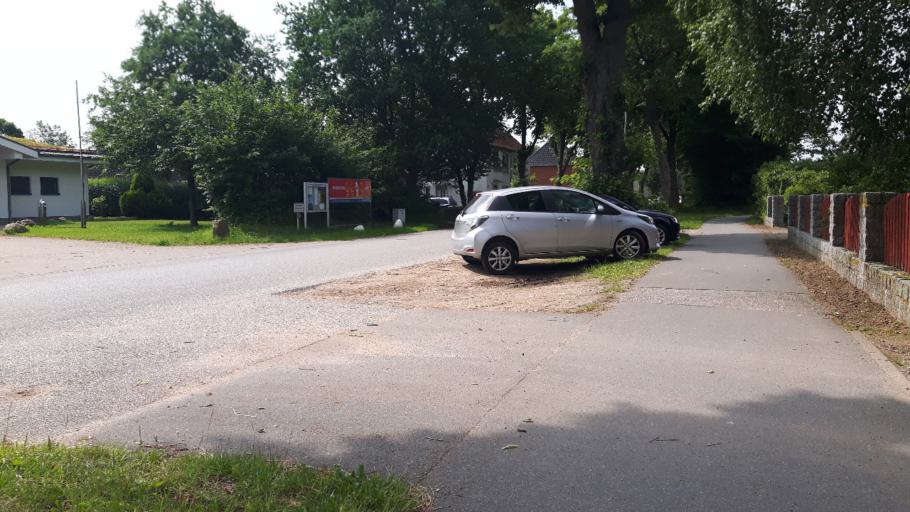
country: DE
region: Schleswig-Holstein
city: Travemuende
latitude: 53.9353
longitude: 10.8388
